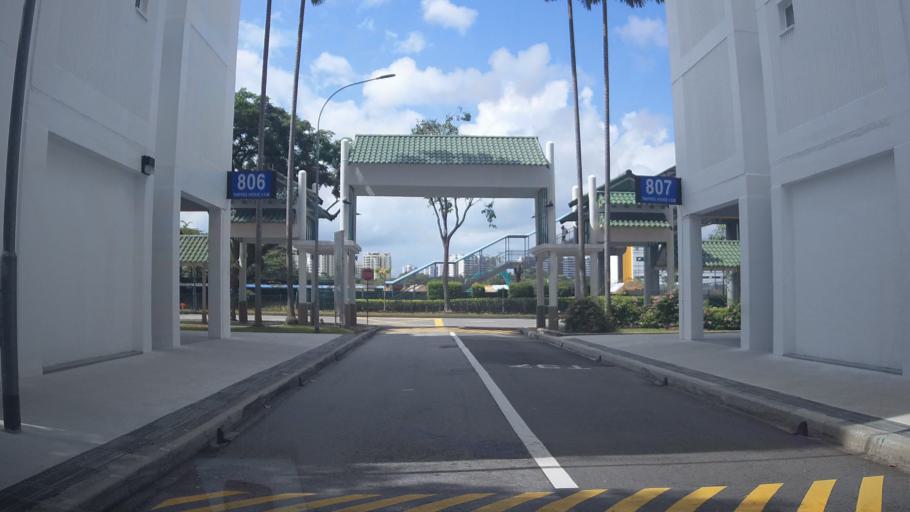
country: SG
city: Singapore
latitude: 1.3459
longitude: 103.9364
